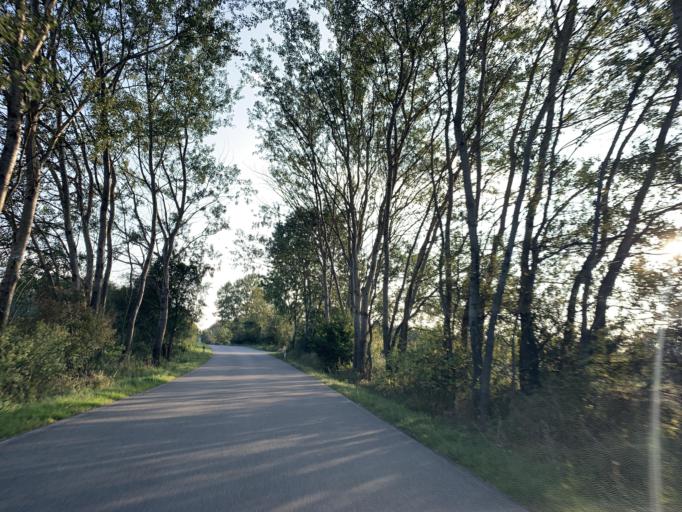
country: DE
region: Mecklenburg-Vorpommern
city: Loitz
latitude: 53.3608
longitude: 13.4368
